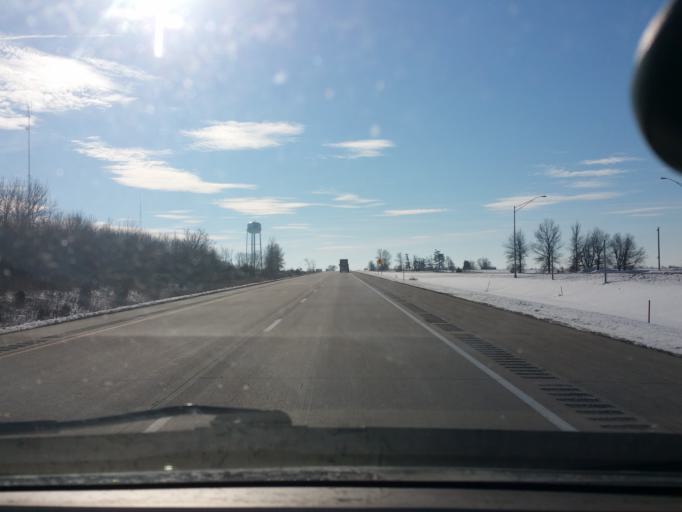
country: US
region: Iowa
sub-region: Clarke County
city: Osceola
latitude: 40.9929
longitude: -93.7990
